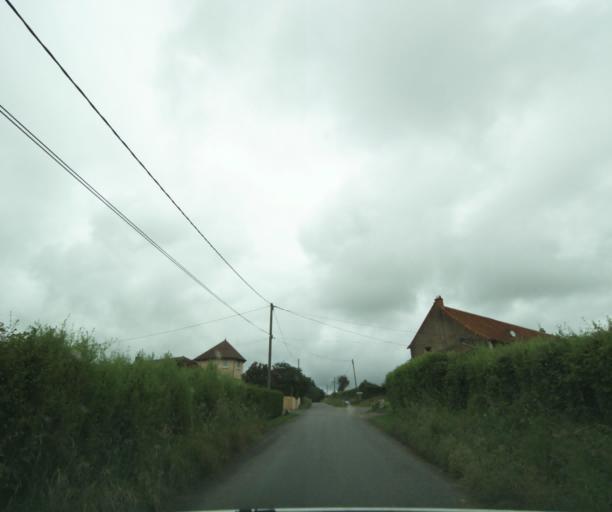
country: FR
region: Bourgogne
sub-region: Departement de Saone-et-Loire
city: Charolles
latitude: 46.4534
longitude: 4.3446
